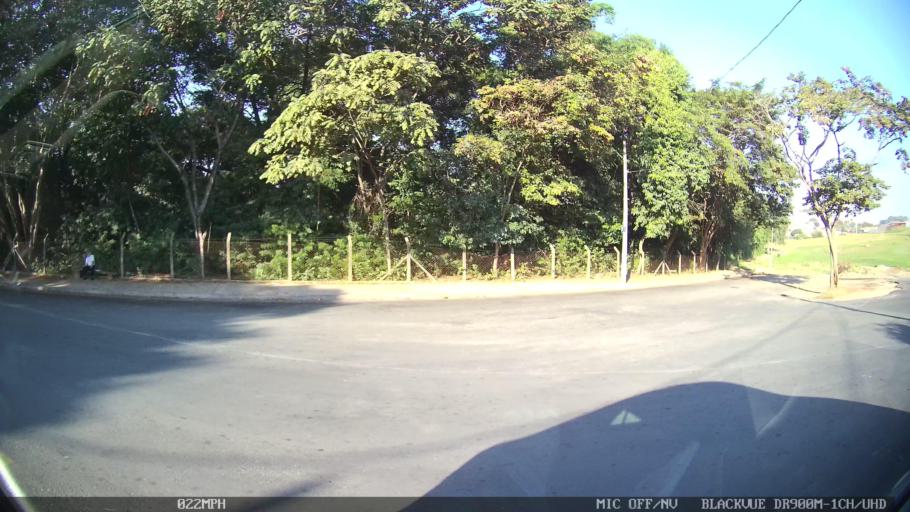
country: BR
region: Sao Paulo
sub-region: Campinas
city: Campinas
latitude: -22.9780
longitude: -47.1456
